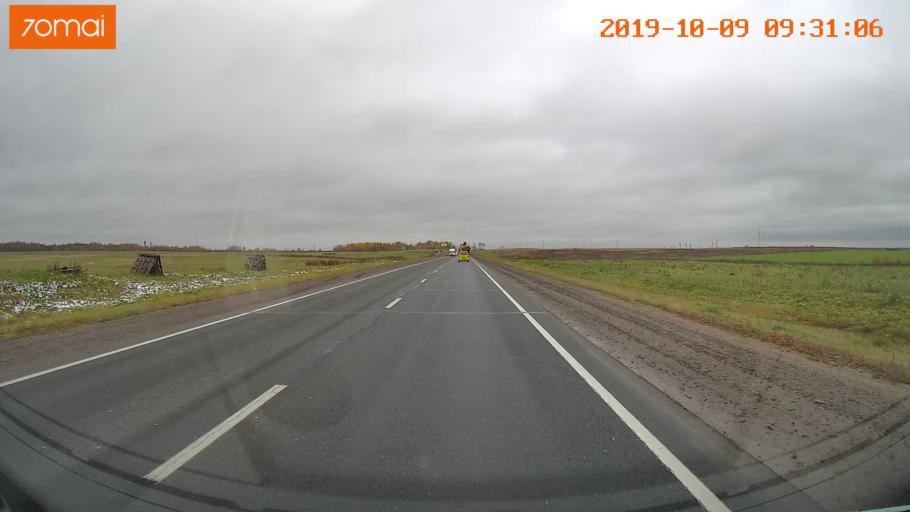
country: RU
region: Vologda
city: Vologda
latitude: 59.1464
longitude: 39.9420
